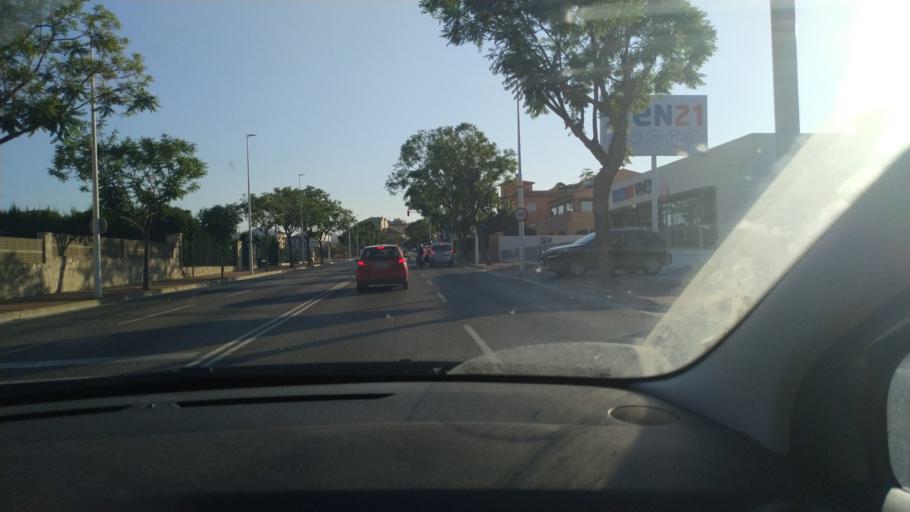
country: ES
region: Valencia
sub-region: Provincia de Alicante
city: Javea
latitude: 38.7875
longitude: 0.1679
